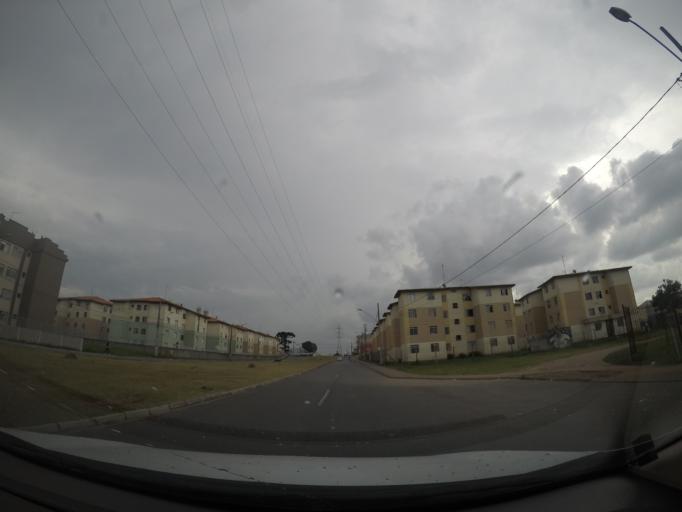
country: BR
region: Parana
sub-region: Sao Jose Dos Pinhais
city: Sao Jose dos Pinhais
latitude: -25.5537
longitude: -49.2489
